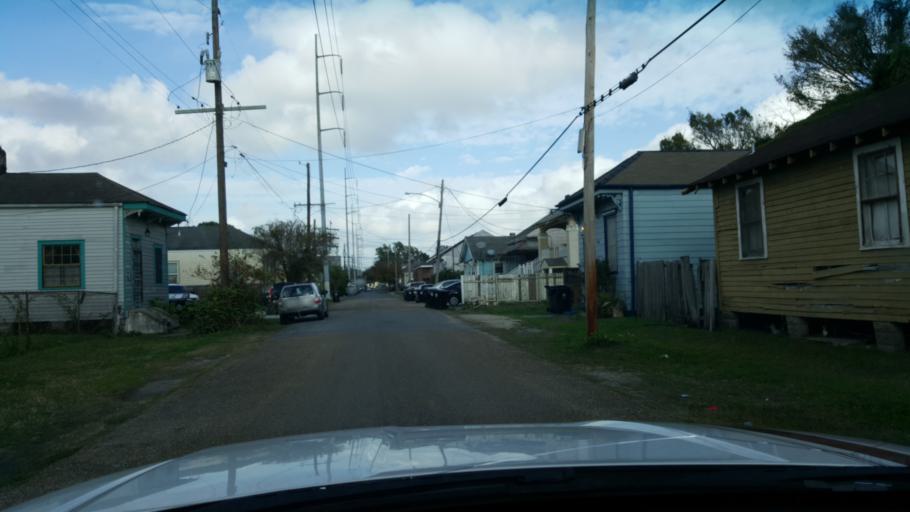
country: US
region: Louisiana
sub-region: Orleans Parish
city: New Orleans
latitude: 29.9768
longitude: -90.0734
